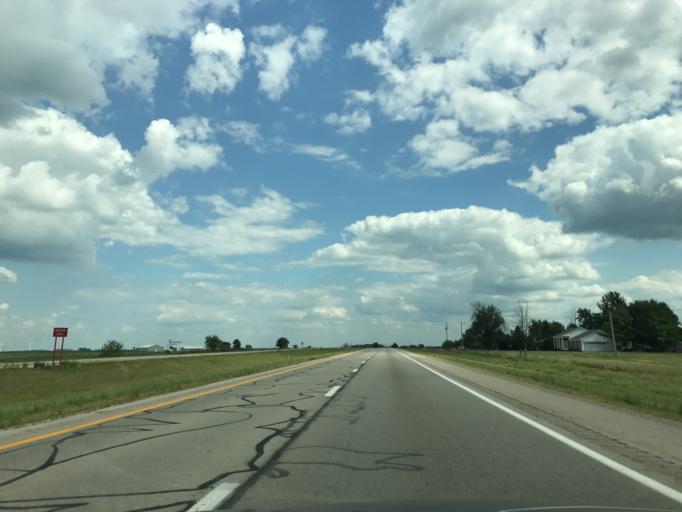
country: US
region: Indiana
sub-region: Allen County
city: Monroeville
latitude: 40.9894
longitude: -84.7837
